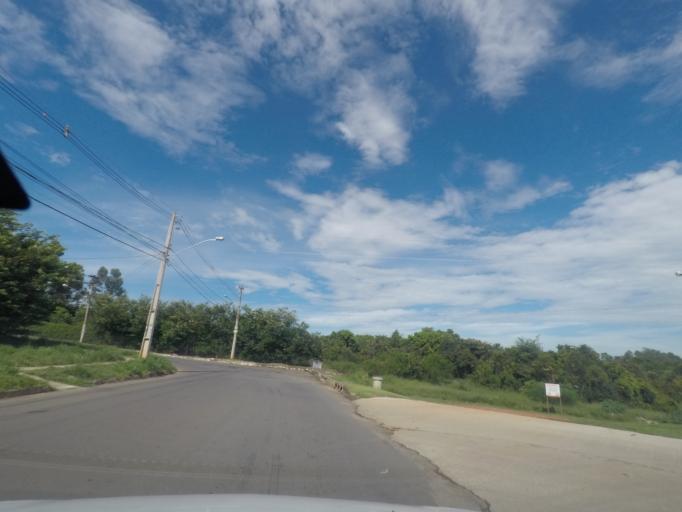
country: BR
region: Goias
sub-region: Aparecida De Goiania
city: Aparecida de Goiania
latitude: -16.7924
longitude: -49.2621
